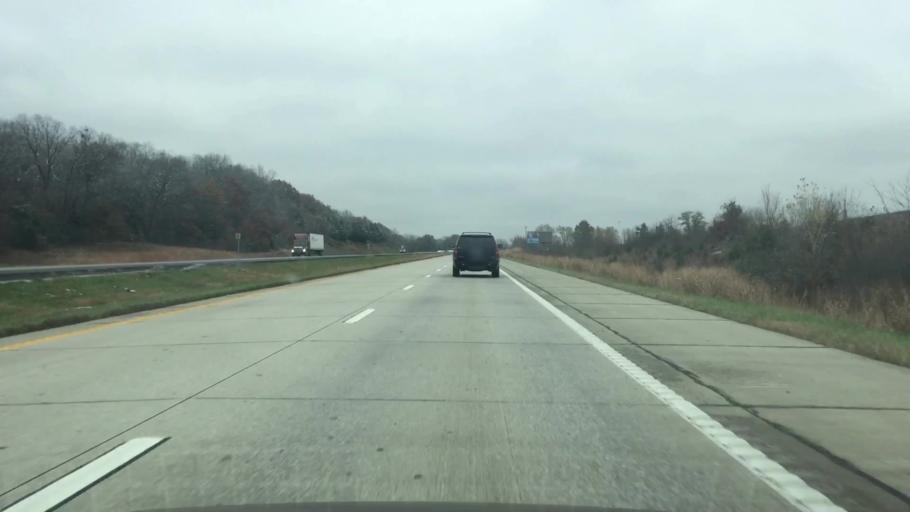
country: US
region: Missouri
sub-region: Saint Clair County
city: Osceola
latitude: 38.0169
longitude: -93.6642
